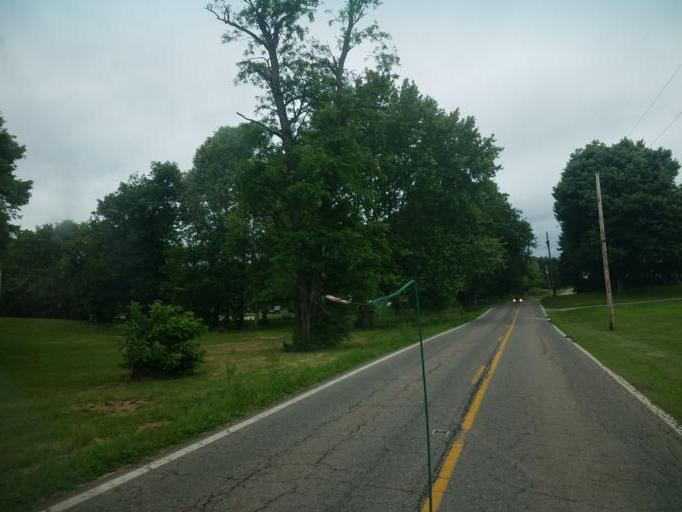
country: US
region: Ohio
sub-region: Columbiana County
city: Columbiana
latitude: 40.8333
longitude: -80.7082
